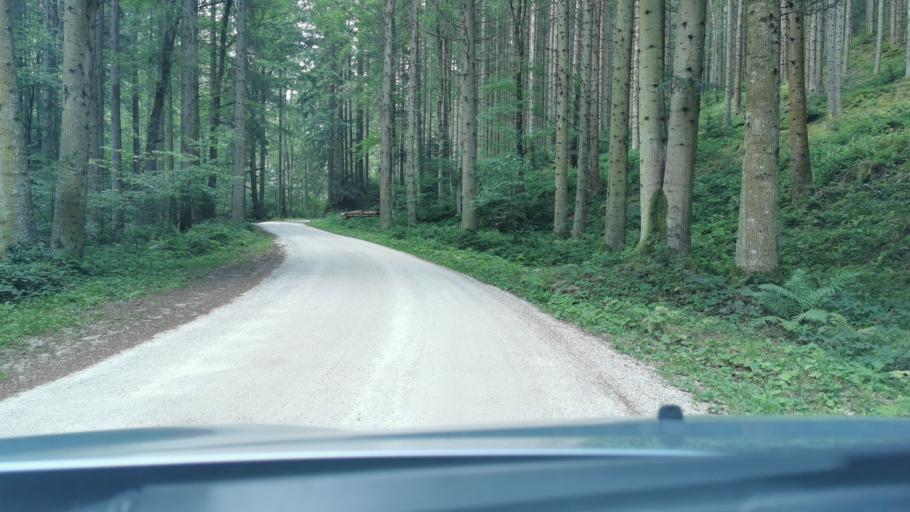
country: AT
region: Styria
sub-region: Politischer Bezirk Weiz
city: Fischbach
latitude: 47.4076
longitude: 15.6408
